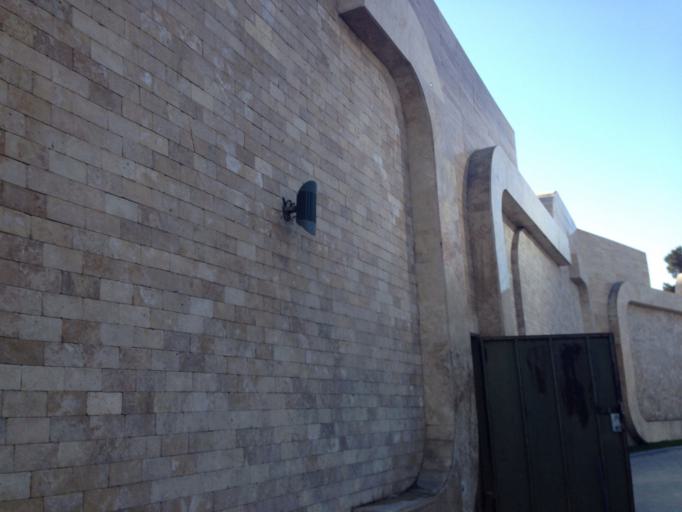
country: AZ
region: Baki
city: Baku
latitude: 40.3745
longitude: 49.8644
